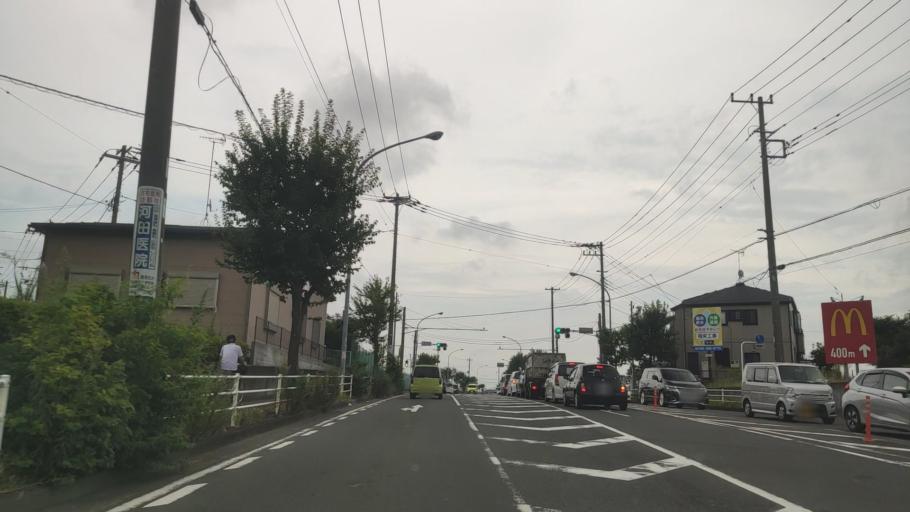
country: JP
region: Kanagawa
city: Minami-rinkan
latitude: 35.4509
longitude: 139.4835
